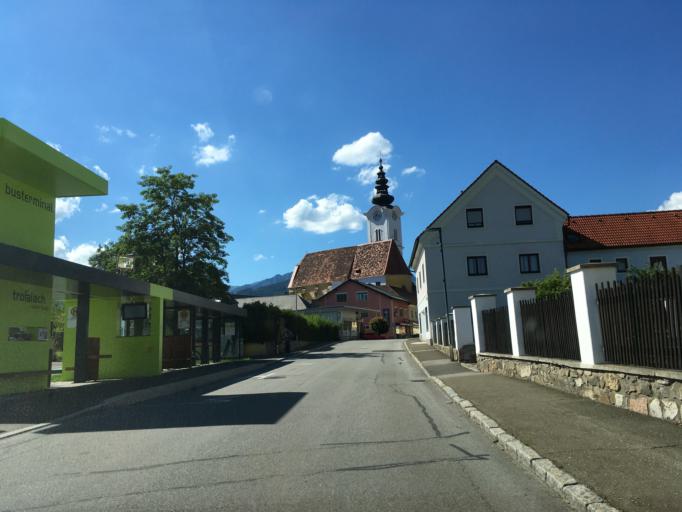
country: AT
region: Styria
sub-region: Politischer Bezirk Leoben
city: Trofaiach
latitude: 47.4244
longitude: 15.0103
